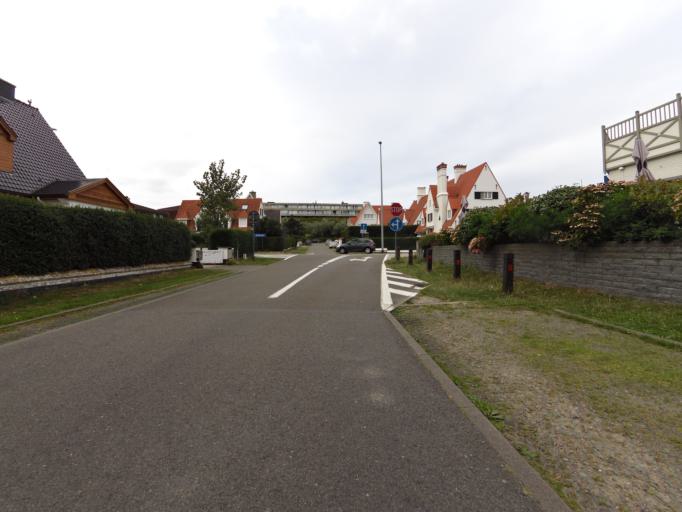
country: BE
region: Flanders
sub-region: Provincie West-Vlaanderen
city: De Haan
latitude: 51.2799
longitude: 3.0387
